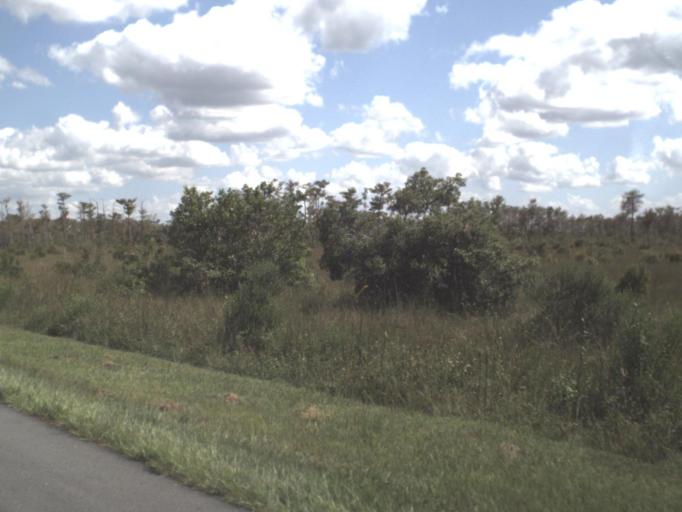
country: US
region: Florida
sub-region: Collier County
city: Marco
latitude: 25.8749
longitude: -81.2111
